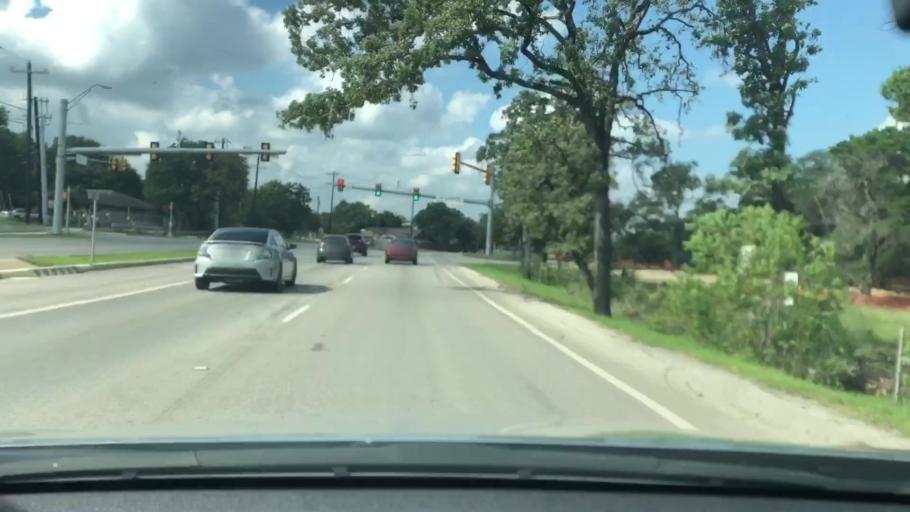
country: US
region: Texas
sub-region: Kendall County
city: Boerne
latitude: 29.7829
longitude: -98.7170
